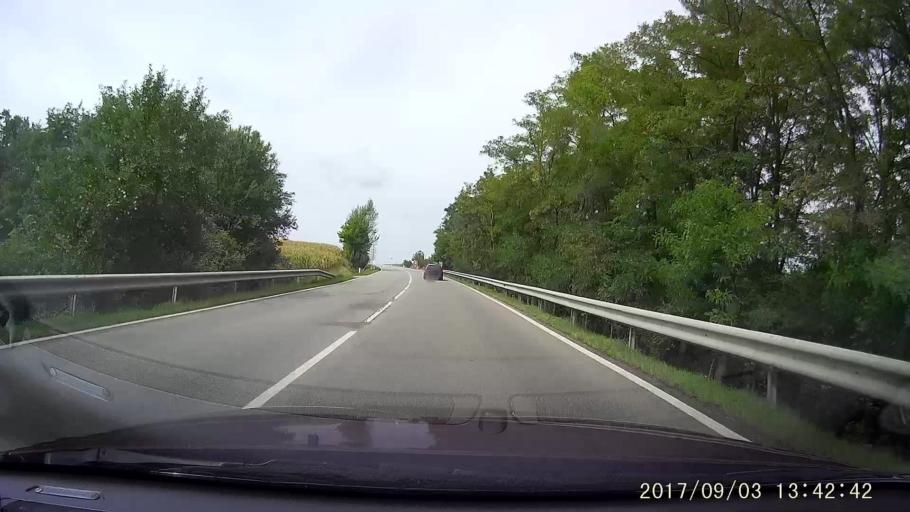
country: AT
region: Lower Austria
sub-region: Politischer Bezirk Hollabrunn
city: Wullersdorf
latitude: 48.6172
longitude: 16.0676
